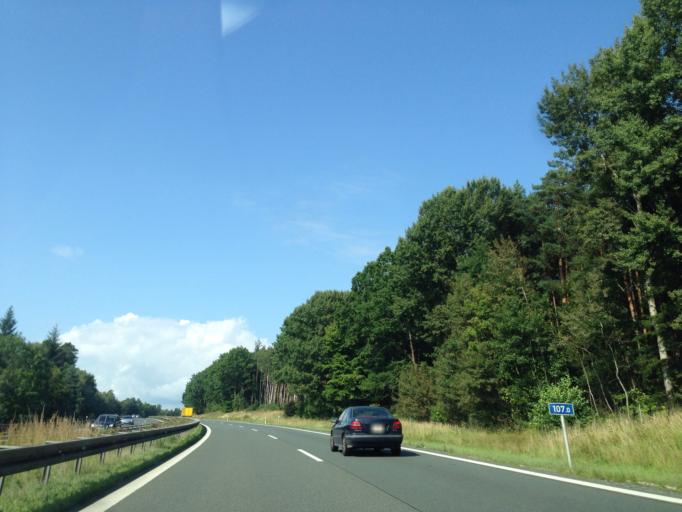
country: DE
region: Bavaria
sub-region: Upper Franconia
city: Eckersdorf
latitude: 50.0262
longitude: 11.4389
